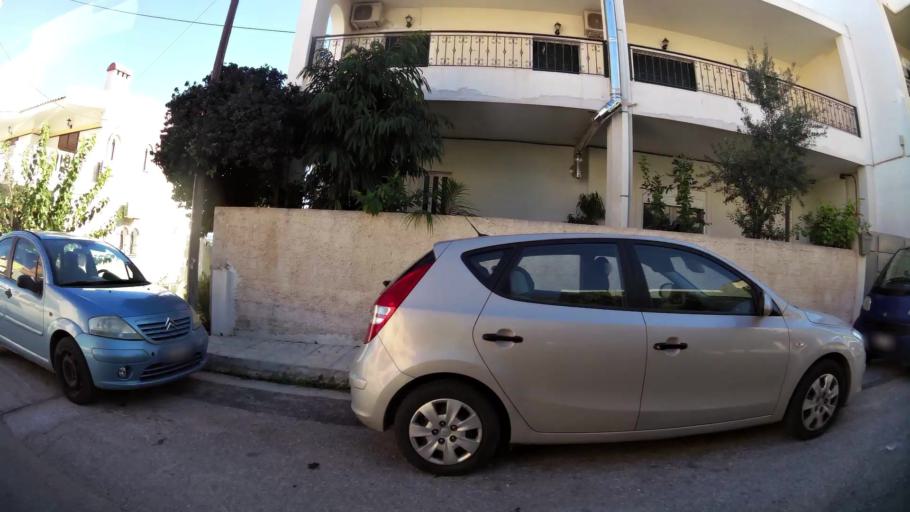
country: GR
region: Attica
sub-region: Nomarchia Anatolikis Attikis
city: Koropi
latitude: 37.9012
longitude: 23.8824
